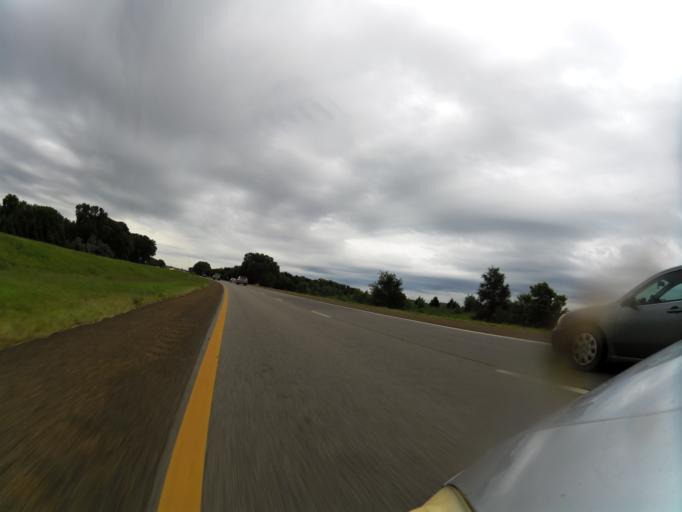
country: US
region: Kansas
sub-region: Sedgwick County
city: Maize
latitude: 37.7596
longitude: -97.4410
